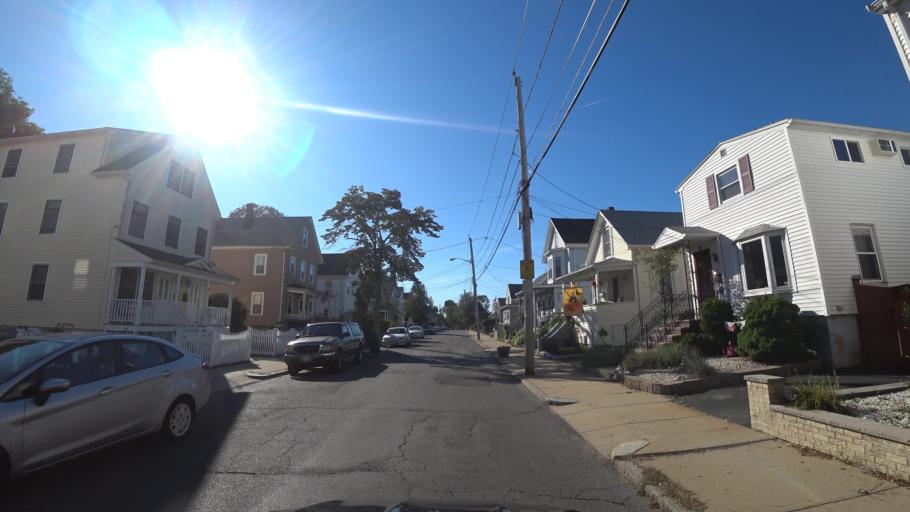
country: US
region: Massachusetts
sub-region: Middlesex County
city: Malden
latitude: 42.4195
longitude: -71.0816
